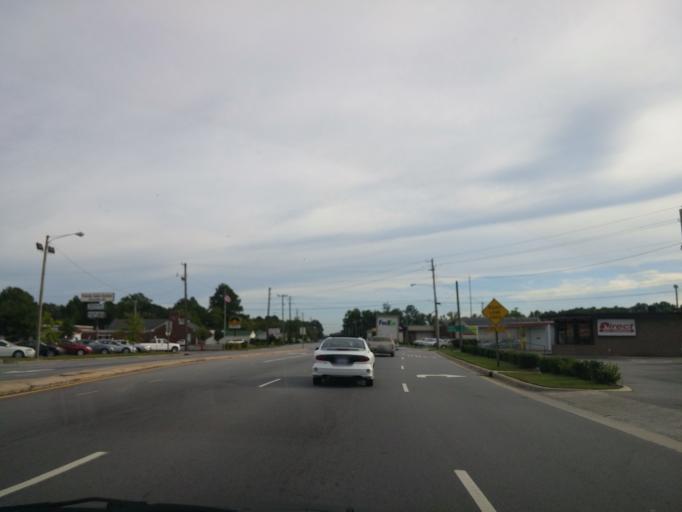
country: US
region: North Carolina
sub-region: Pitt County
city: Summerfield
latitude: 35.5987
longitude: -77.3951
